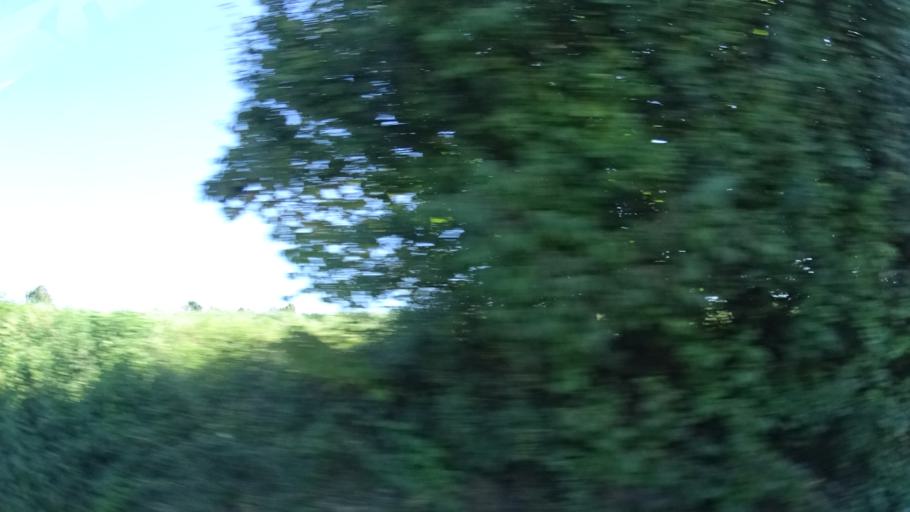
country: DE
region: Baden-Wuerttemberg
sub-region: Karlsruhe Region
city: Konigsbach-Stein
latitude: 48.9719
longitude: 8.6366
